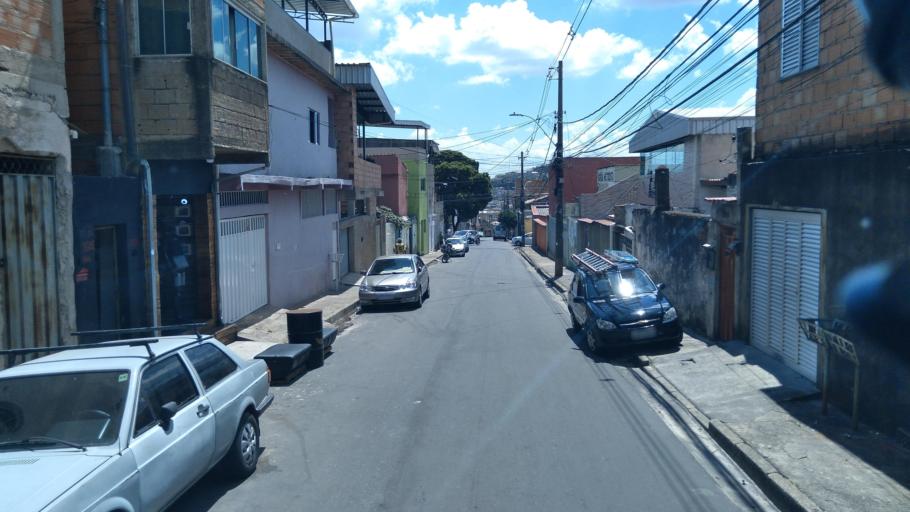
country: BR
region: Minas Gerais
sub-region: Belo Horizonte
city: Belo Horizonte
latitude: -19.9099
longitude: -43.8893
